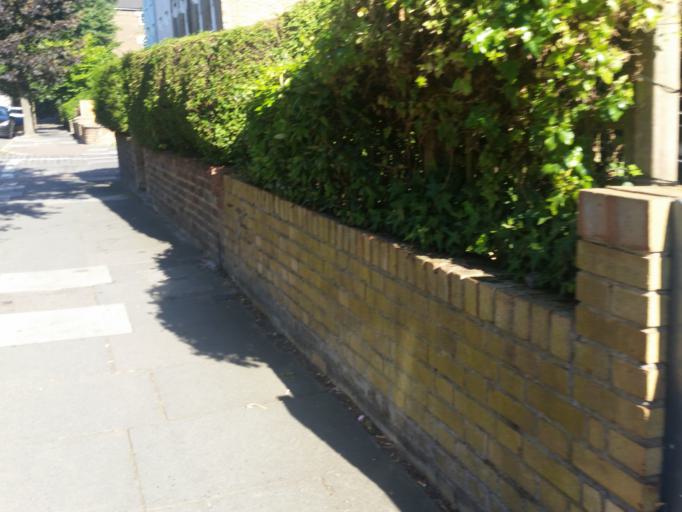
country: GB
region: England
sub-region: Greater London
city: Crouch End
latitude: 51.5833
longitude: -0.1251
